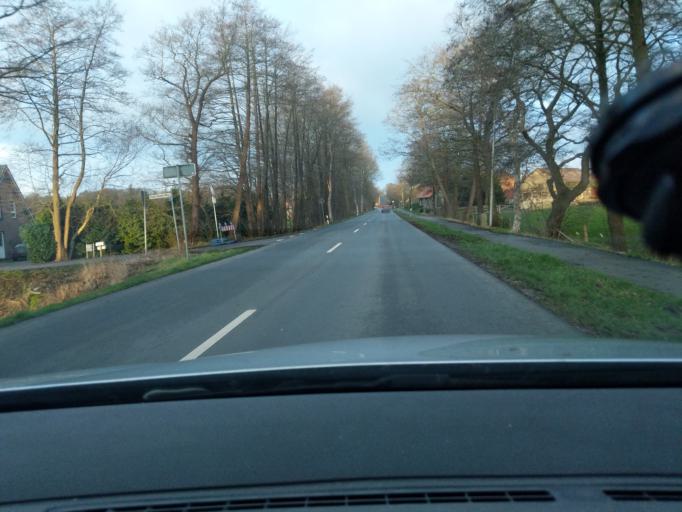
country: DE
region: Lower Saxony
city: Drangstedt
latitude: 53.6753
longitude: 8.6979
